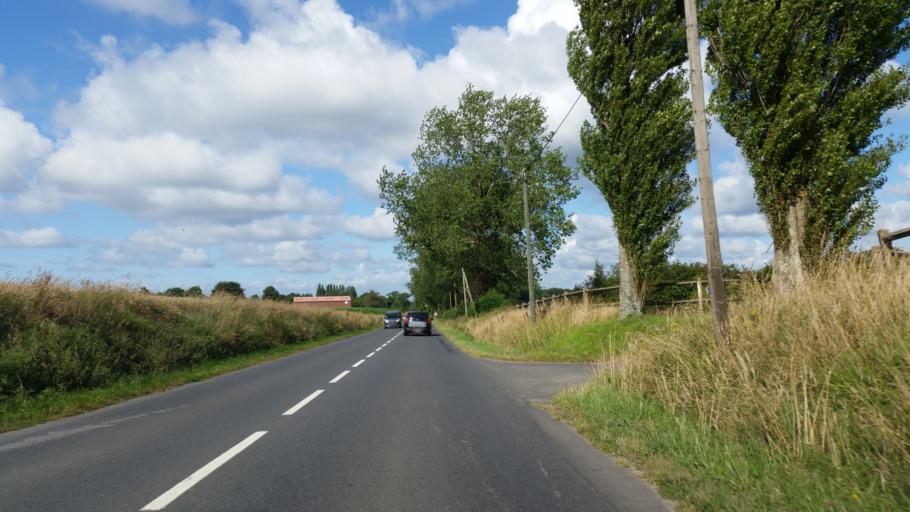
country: FR
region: Lower Normandy
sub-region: Departement du Calvados
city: Villers-sur-Mer
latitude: 49.2842
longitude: 0.0043
